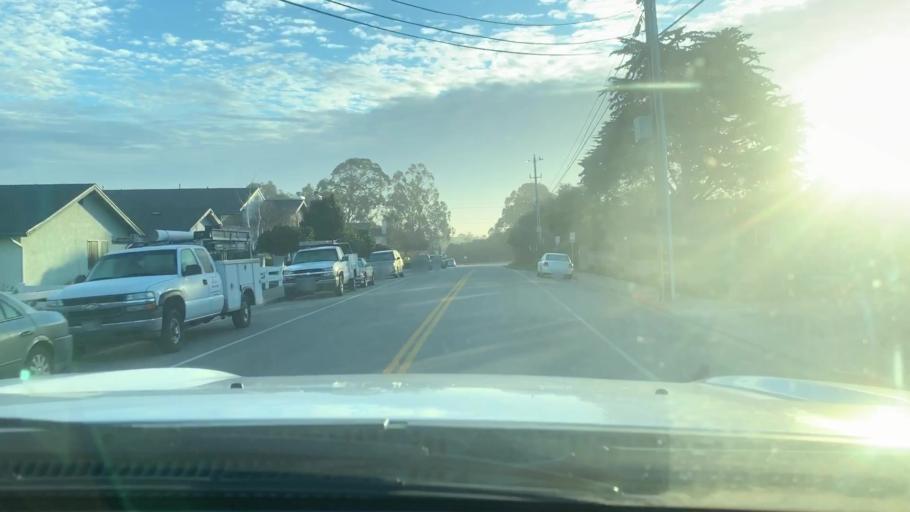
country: US
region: California
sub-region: San Luis Obispo County
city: Los Osos
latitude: 35.3128
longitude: -120.8261
